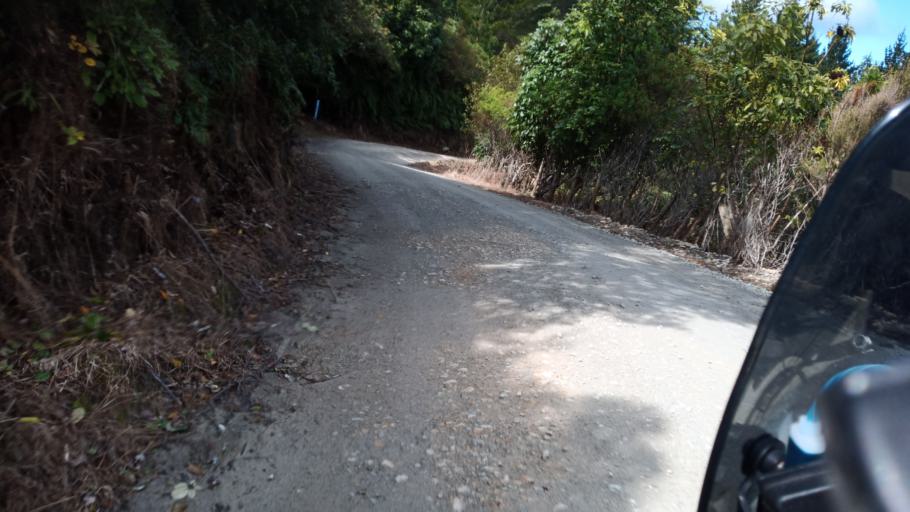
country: NZ
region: Gisborne
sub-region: Gisborne District
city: Gisborne
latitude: -38.8553
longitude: 177.7951
